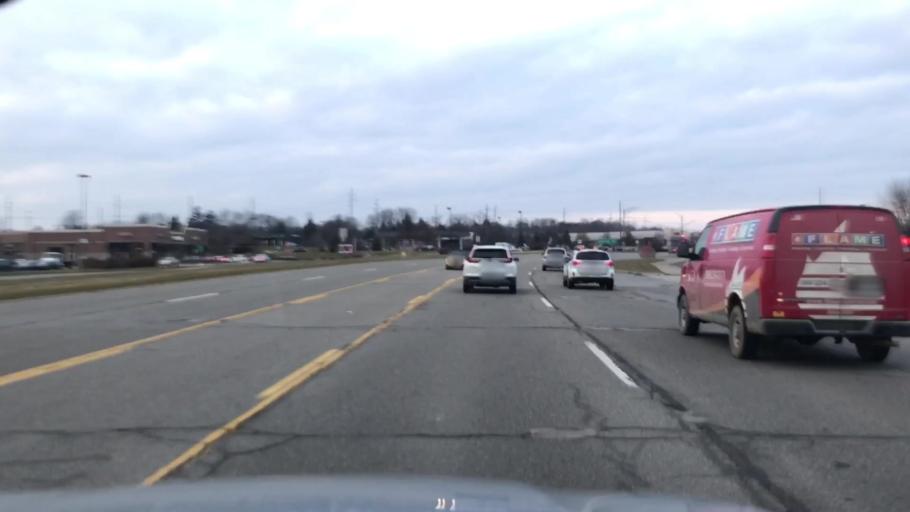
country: US
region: Michigan
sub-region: Wayne County
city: Northville
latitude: 42.4366
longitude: -83.4350
